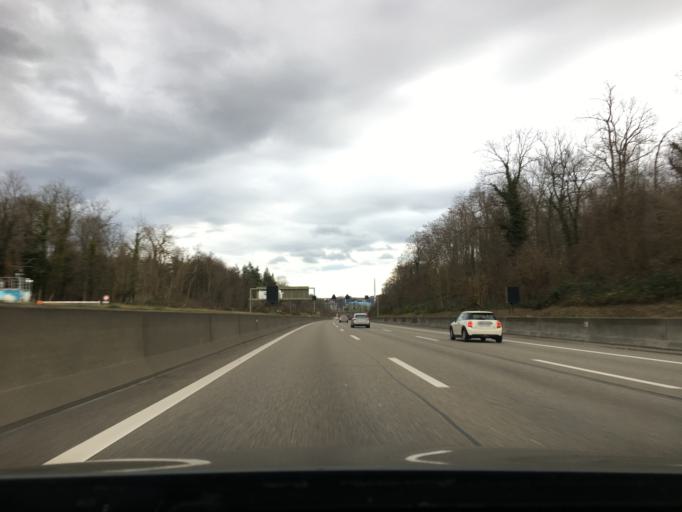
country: CH
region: Basel-Landschaft
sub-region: Bezirk Arlesheim
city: Muttenz
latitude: 47.5380
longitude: 7.6482
